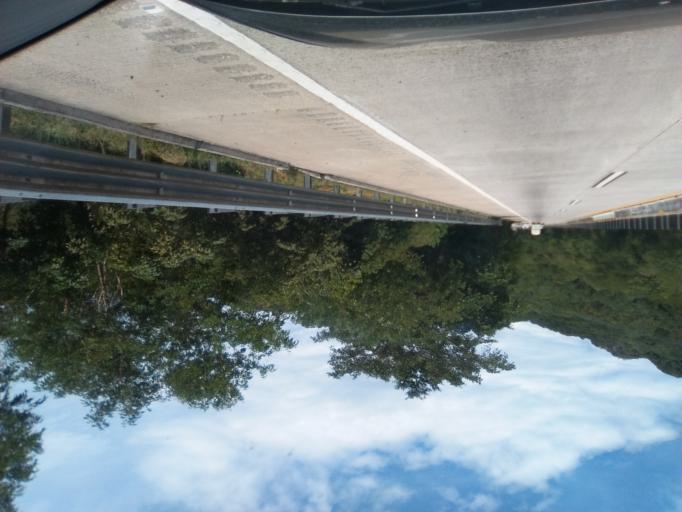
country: MX
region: Guerrero
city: Tierra Colorada
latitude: 17.1066
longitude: -99.5815
